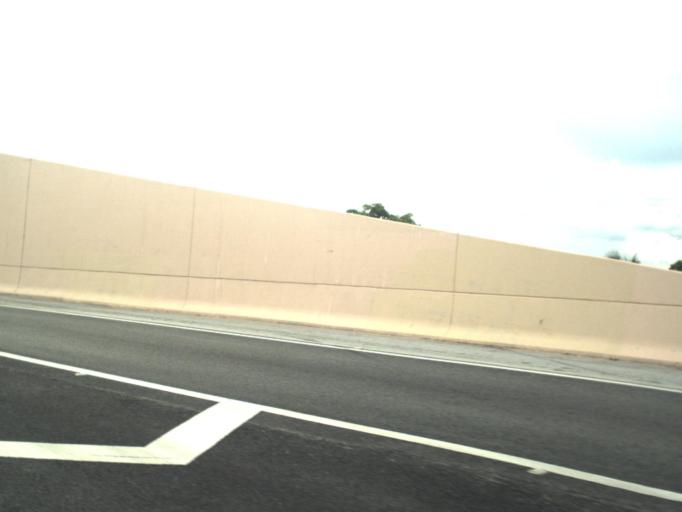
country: US
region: Florida
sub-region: Miami-Dade County
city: Sunset
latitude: 25.6954
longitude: -80.3445
